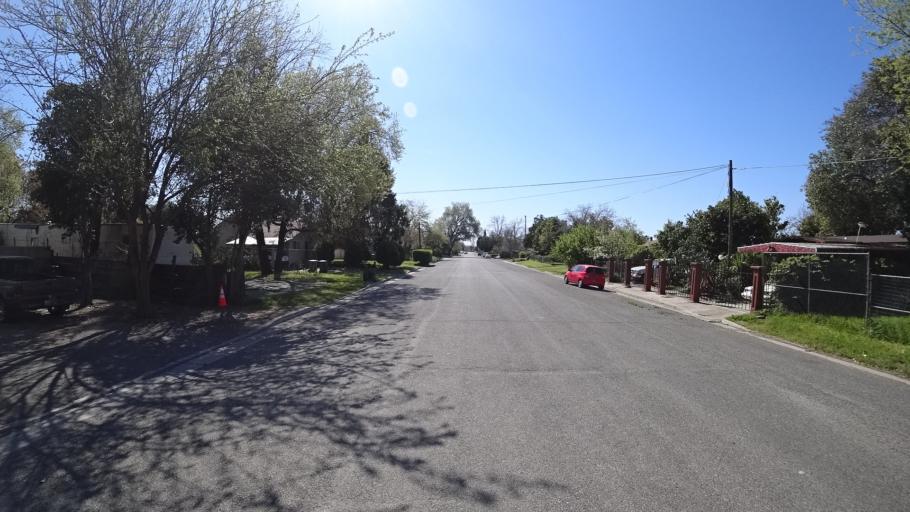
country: US
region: California
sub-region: Glenn County
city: Hamilton City
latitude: 39.7434
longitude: -122.0089
